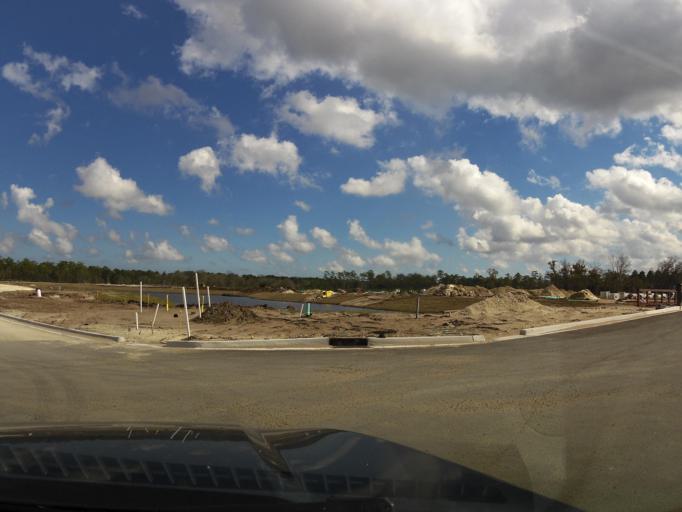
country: US
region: Florida
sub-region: Saint Johns County
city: Ponte Vedra Beach
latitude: 30.2439
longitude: -81.4945
